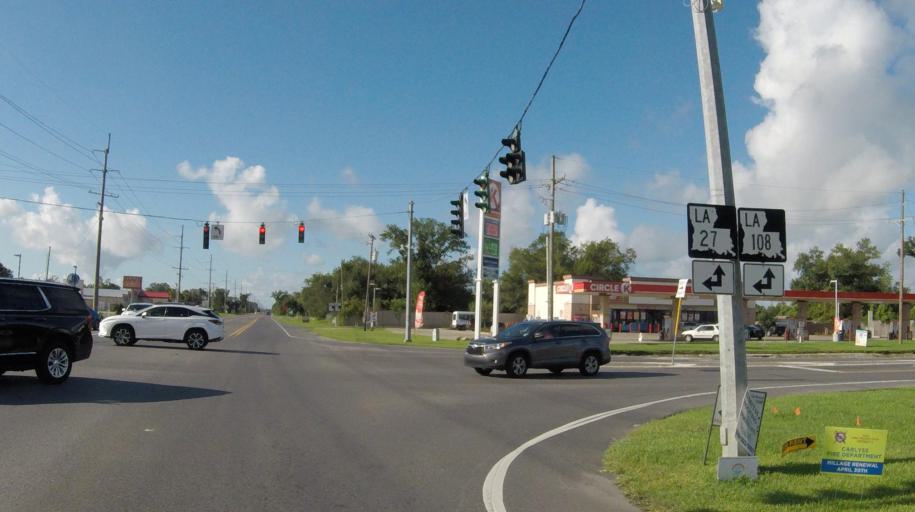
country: US
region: Louisiana
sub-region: Calcasieu Parish
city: Carlyss
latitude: 30.1838
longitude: -93.3762
